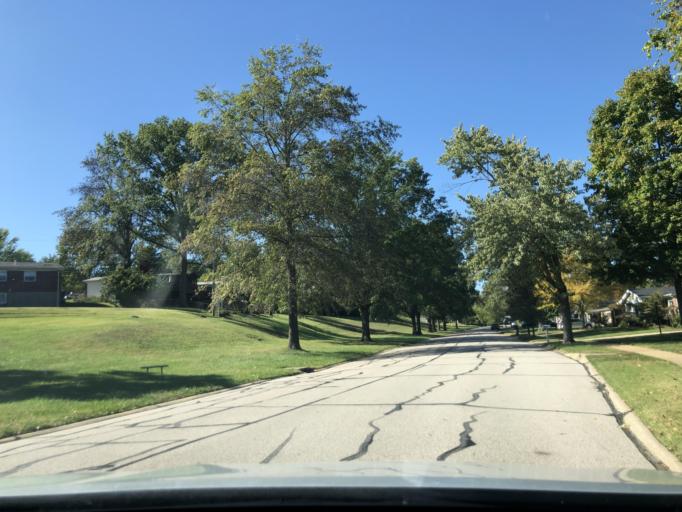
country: US
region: Missouri
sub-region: Saint Louis County
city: Concord
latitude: 38.4977
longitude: -90.3680
